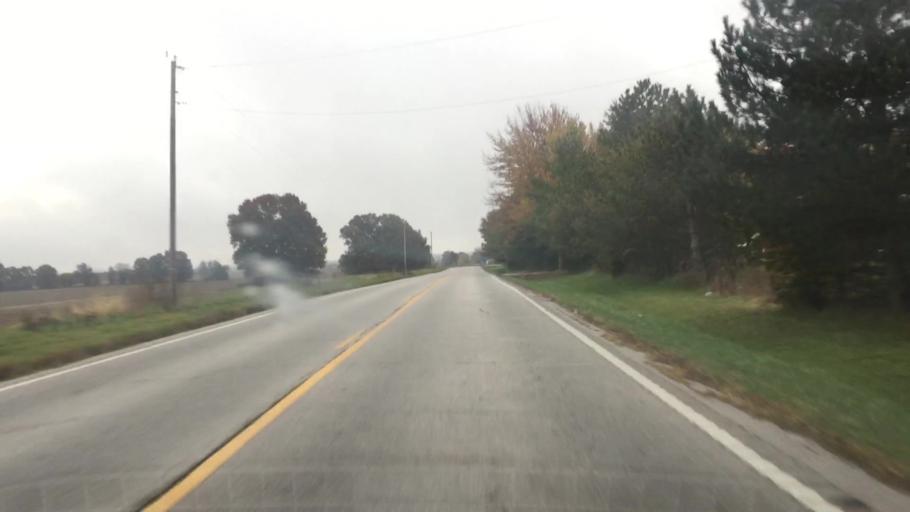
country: US
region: Missouri
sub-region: Boone County
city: Columbia
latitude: 38.9199
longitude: -92.1952
